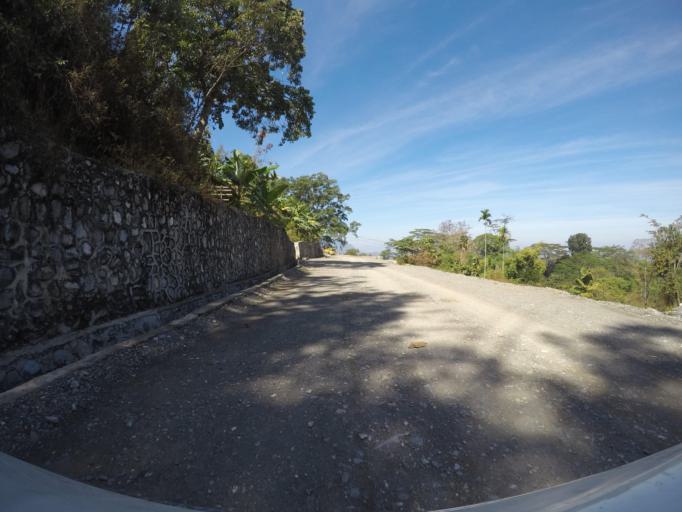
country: TL
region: Ermera
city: Gleno
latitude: -8.8095
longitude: 125.3185
